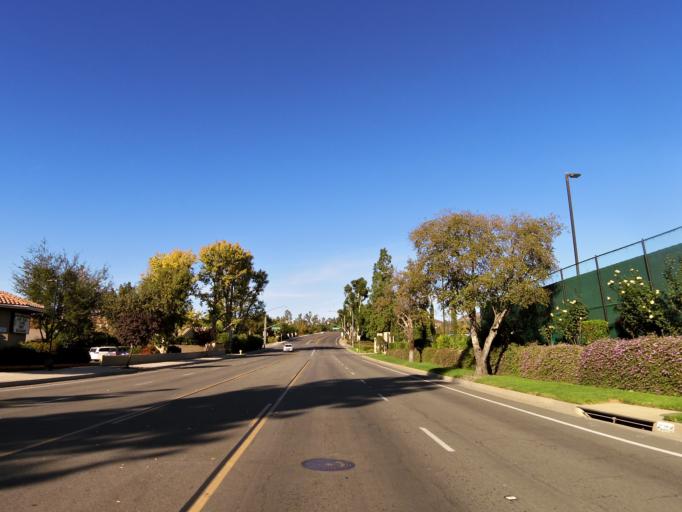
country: US
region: California
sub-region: Los Angeles County
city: Westlake Village
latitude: 34.1490
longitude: -118.8190
